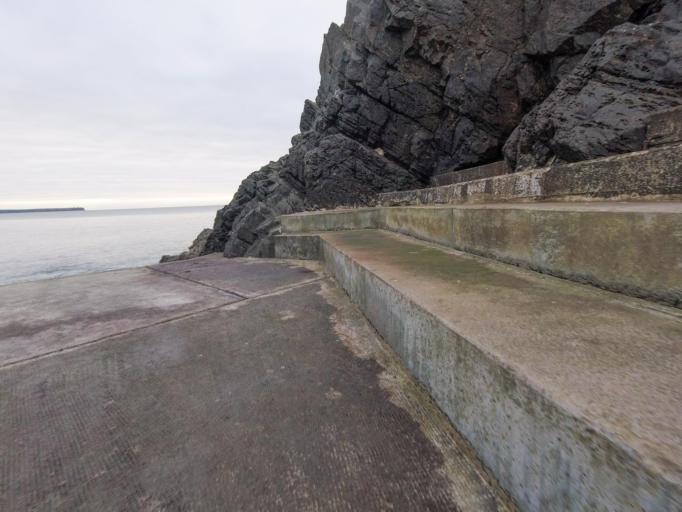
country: IE
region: Munster
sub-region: Waterford
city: Tra Mhor
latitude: 52.1430
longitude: -7.1661
